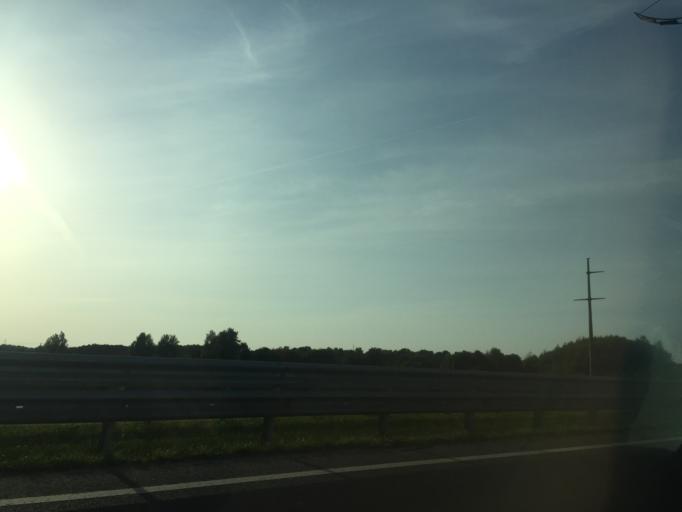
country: RU
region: Kaliningrad
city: Maloye Isakovo
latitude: 54.7546
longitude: 20.5845
